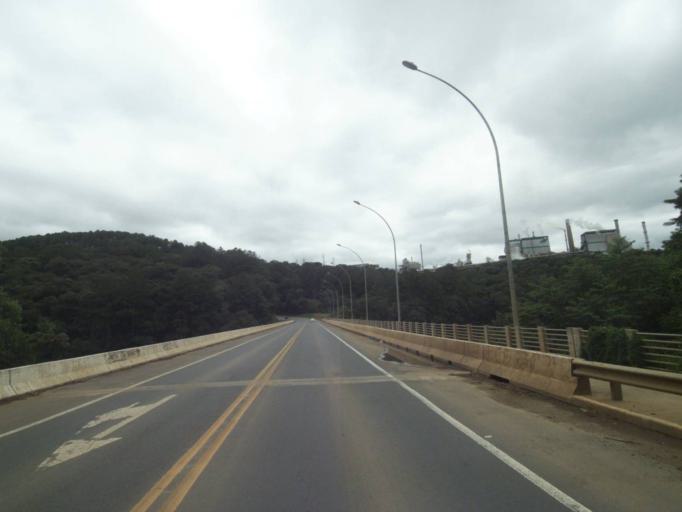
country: BR
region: Parana
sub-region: Telemaco Borba
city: Telemaco Borba
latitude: -24.3130
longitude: -50.6161
